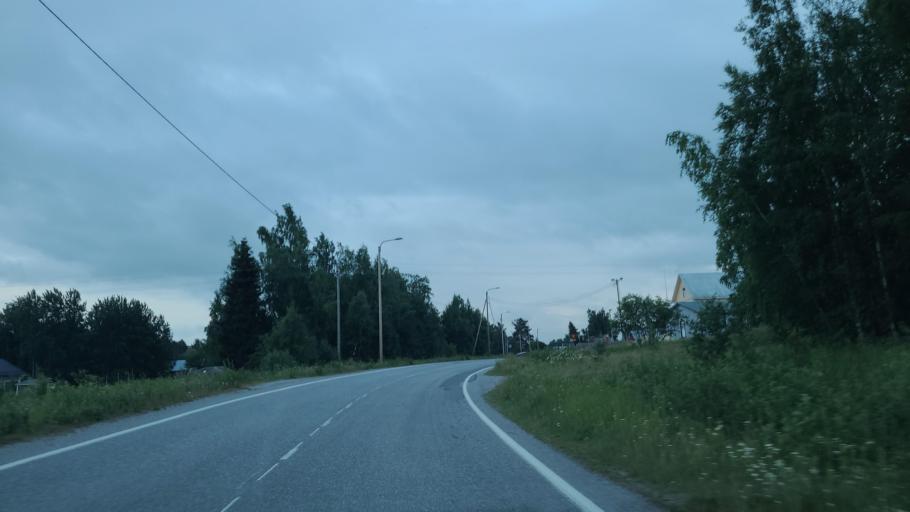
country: FI
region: Ostrobothnia
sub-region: Vaasa
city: Replot
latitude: 63.1988
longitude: 21.3039
